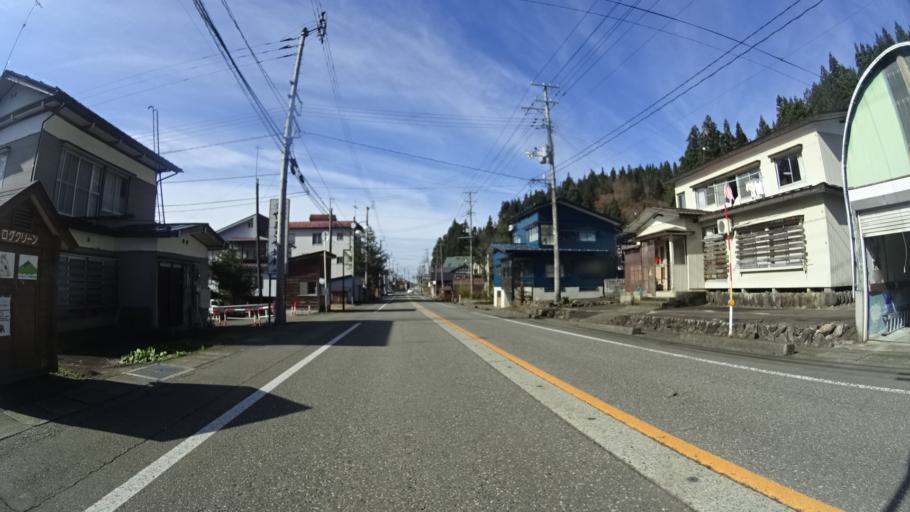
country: JP
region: Niigata
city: Muikamachi
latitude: 37.2075
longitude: 139.0641
